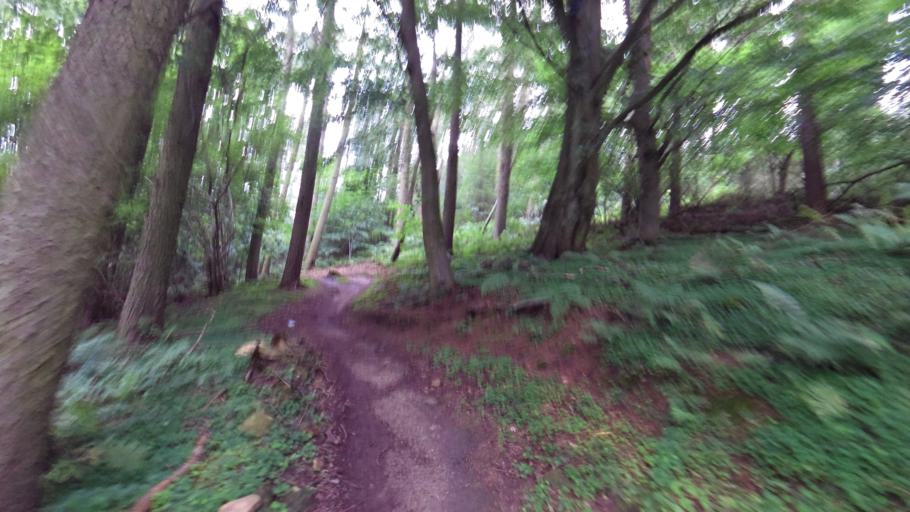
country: GB
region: England
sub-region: North Yorkshire
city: Thornton Dale
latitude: 54.2811
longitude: -0.6869
